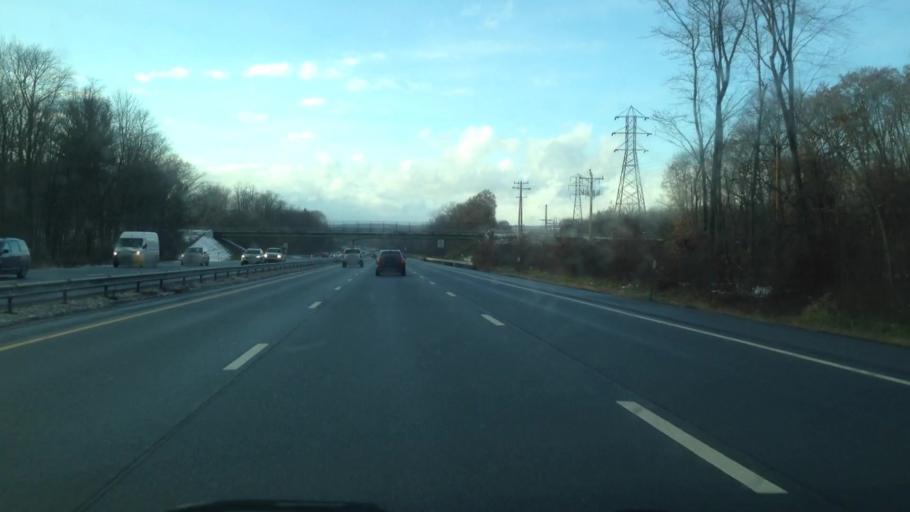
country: US
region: New York
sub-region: Schenectady County
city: Rotterdam
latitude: 42.7707
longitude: -73.9726
